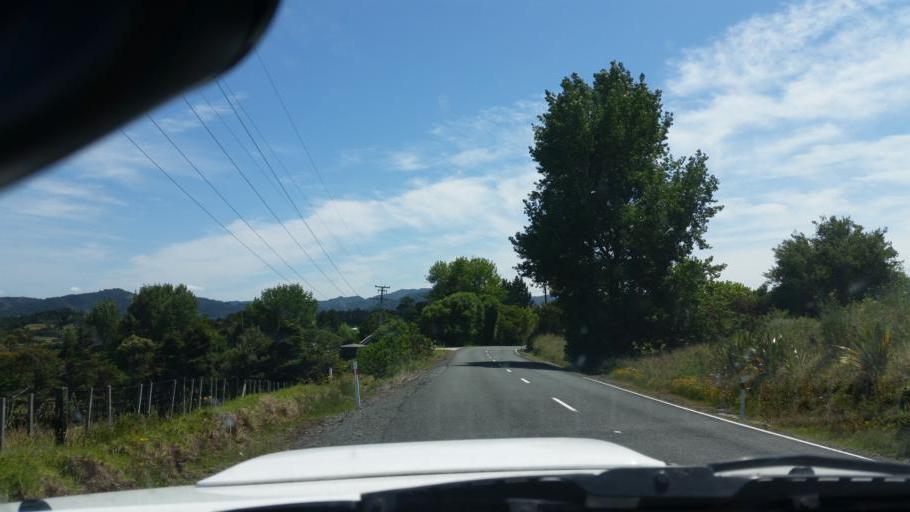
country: NZ
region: Auckland
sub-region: Auckland
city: Wellsford
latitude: -36.1799
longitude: 174.4126
